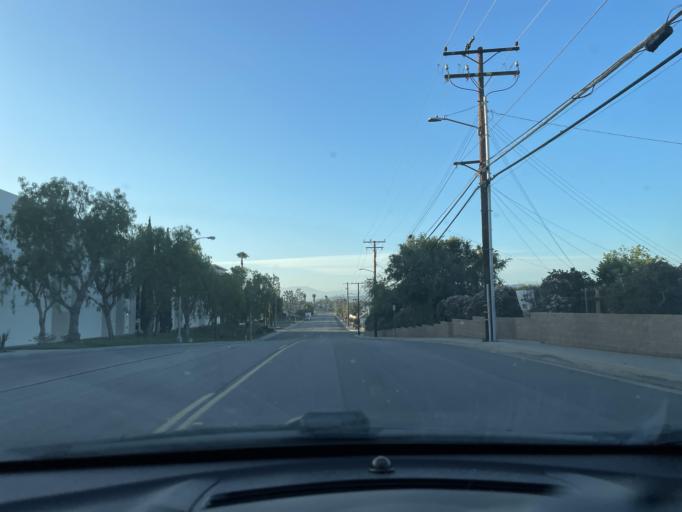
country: US
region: California
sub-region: Los Angeles County
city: La Mirada
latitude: 33.9118
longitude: -118.0380
